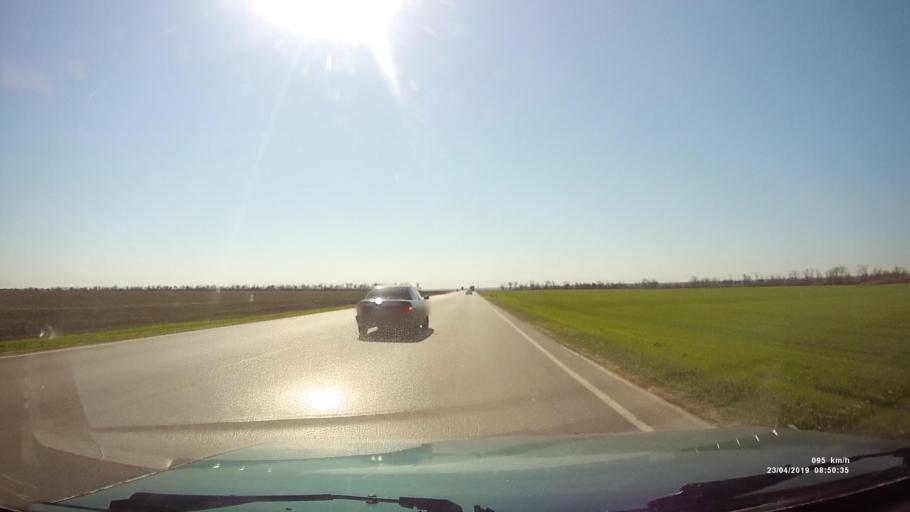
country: RU
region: Rostov
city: Gigant
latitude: 46.4951
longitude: 41.4307
